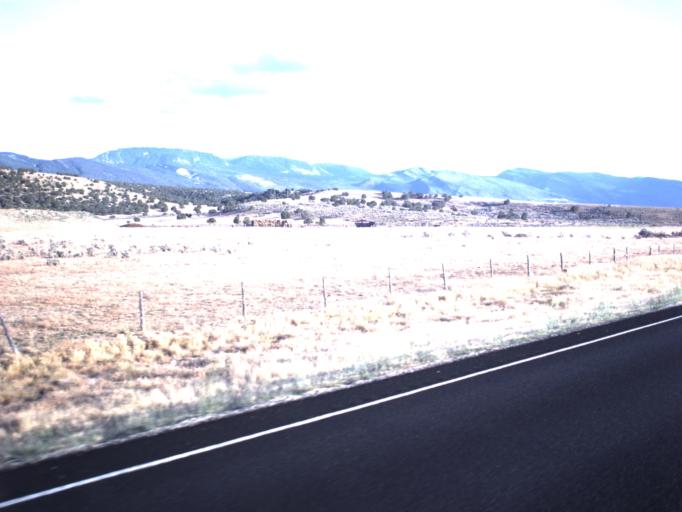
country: US
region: Utah
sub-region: Sanpete County
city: Ephraim
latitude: 39.4266
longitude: -111.5568
